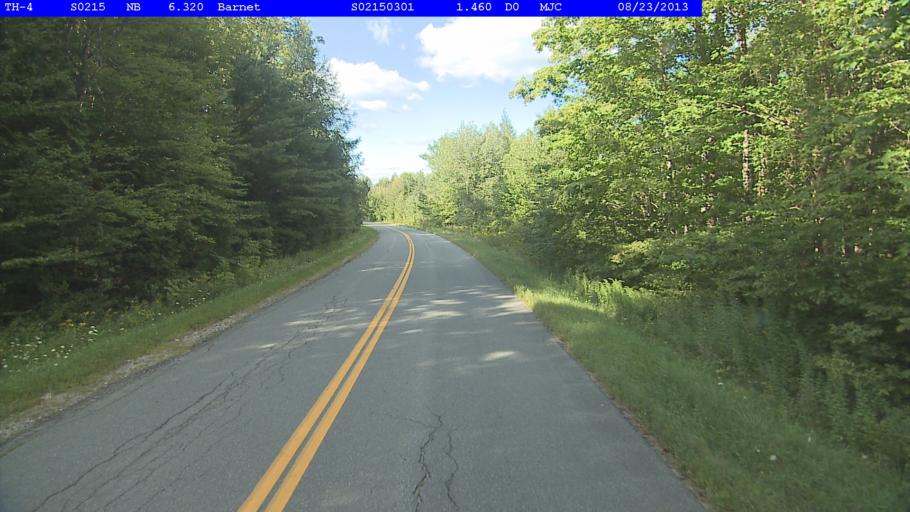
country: US
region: New Hampshire
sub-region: Grafton County
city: Woodsville
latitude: 44.2930
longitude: -72.1630
